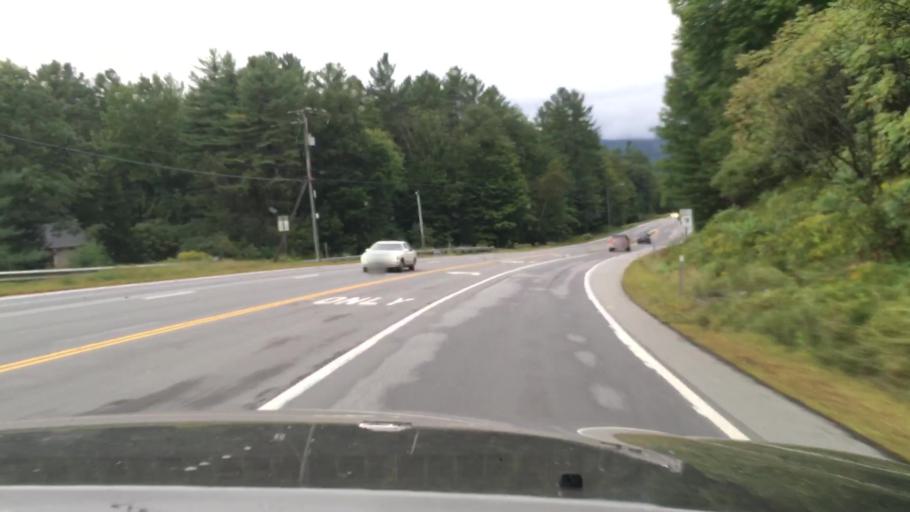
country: US
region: New Hampshire
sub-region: Cheshire County
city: Chesterfield
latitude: 42.8922
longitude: -72.4993
